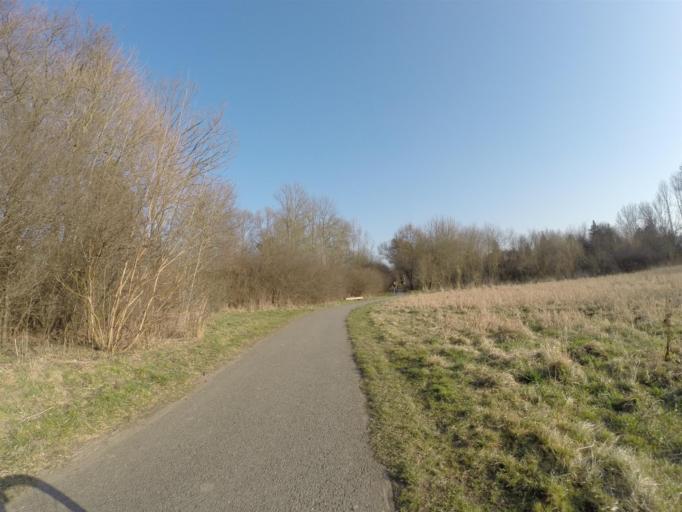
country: DE
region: Thuringia
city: Weimar
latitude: 50.9623
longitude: 11.3495
